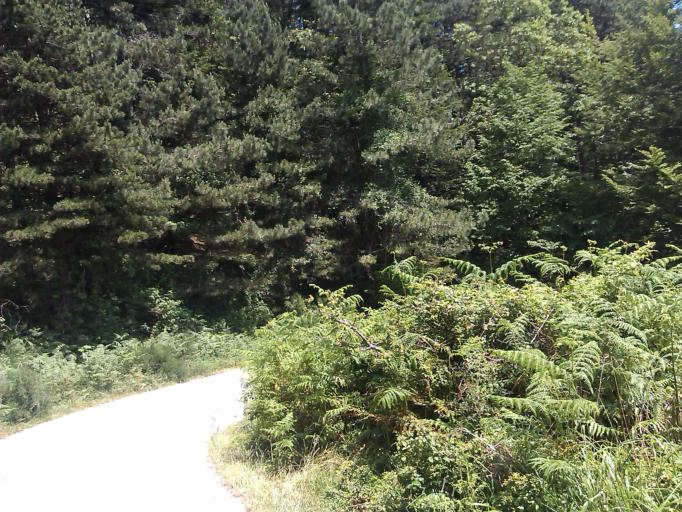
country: IT
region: Tuscany
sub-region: Provincia di Prato
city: Cantagallo
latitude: 43.9923
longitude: 11.0390
